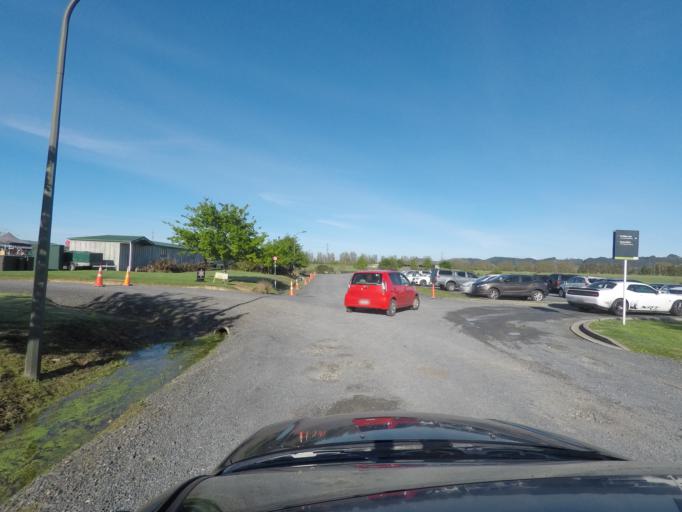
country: NZ
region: Auckland
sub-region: Auckland
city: Red Hill
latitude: -37.0044
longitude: 175.0424
